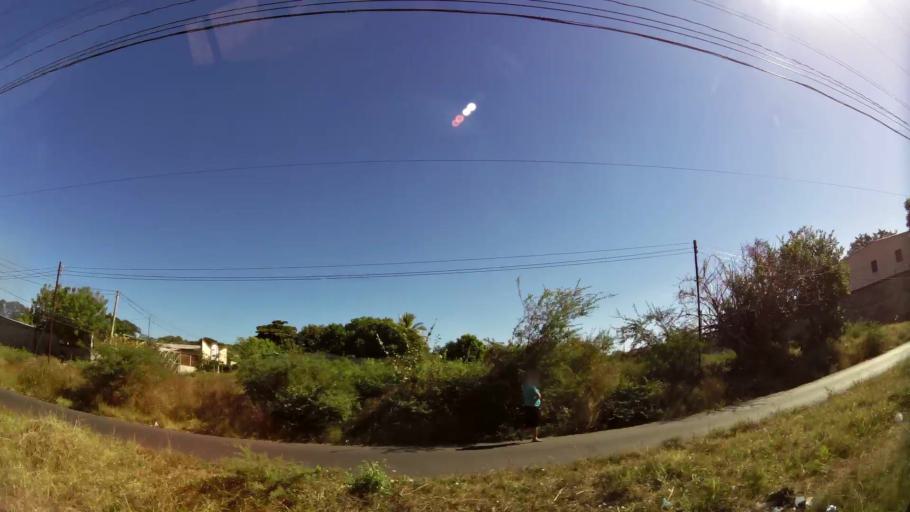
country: SV
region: San Miguel
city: San Miguel
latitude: 13.4660
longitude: -88.1553
